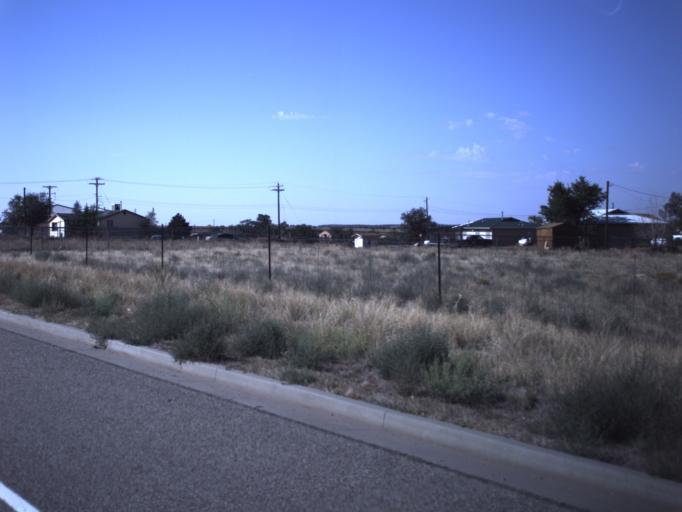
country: US
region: Utah
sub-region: San Juan County
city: Blanding
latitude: 37.4670
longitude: -109.4670
